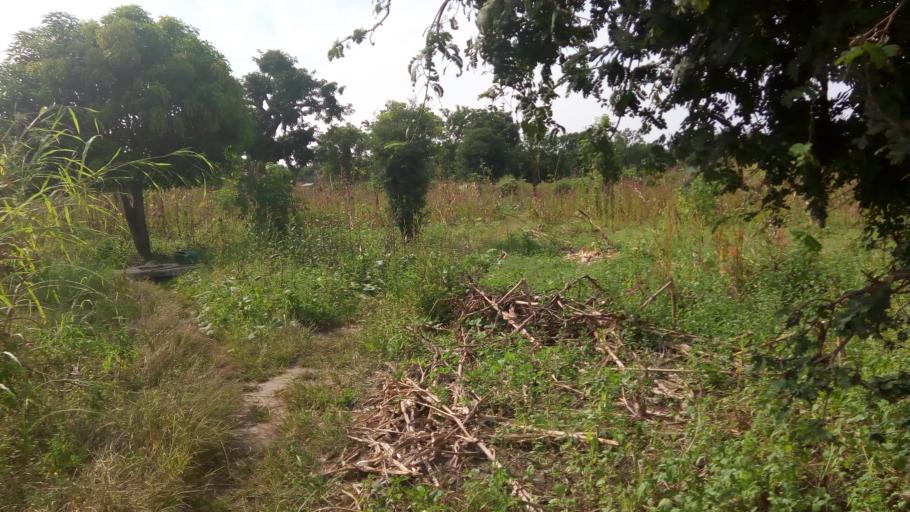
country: ML
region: Koulikoro
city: Kangaba
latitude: 11.6811
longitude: -8.7108
